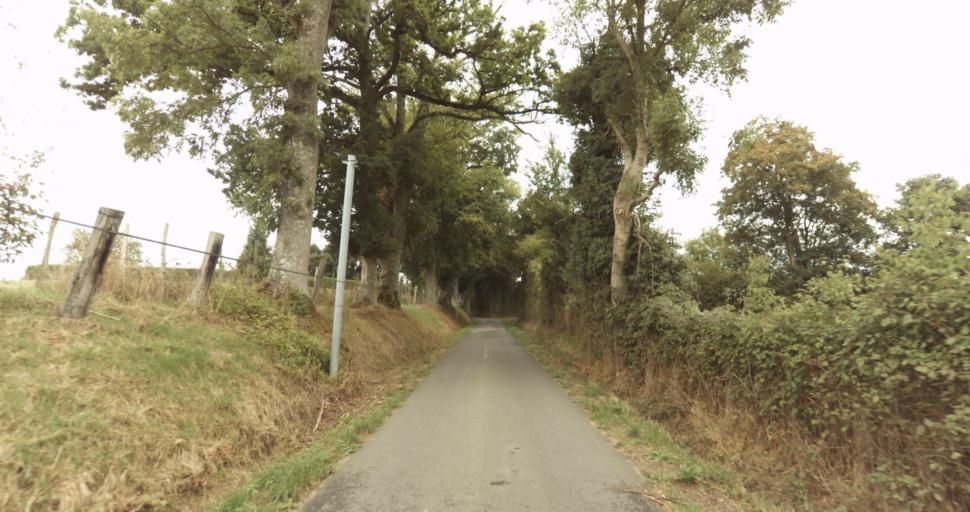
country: FR
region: Lower Normandy
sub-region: Departement de l'Orne
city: Sees
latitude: 48.6725
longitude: 0.2618
